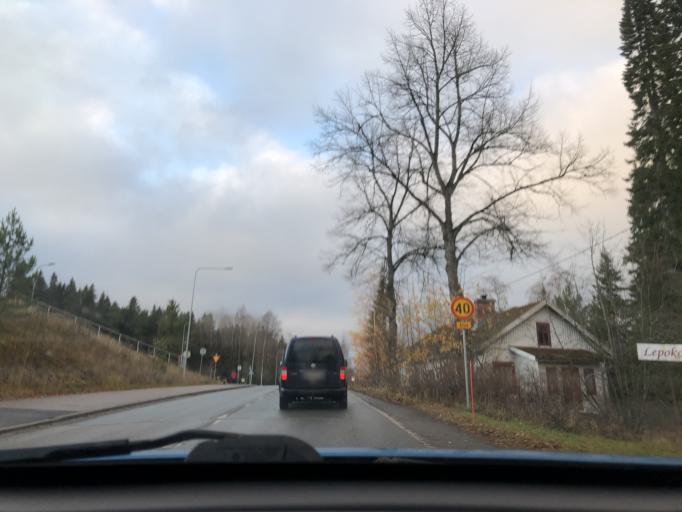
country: FI
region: Pirkanmaa
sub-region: Tampere
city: Kangasala
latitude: 61.4671
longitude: 24.0653
